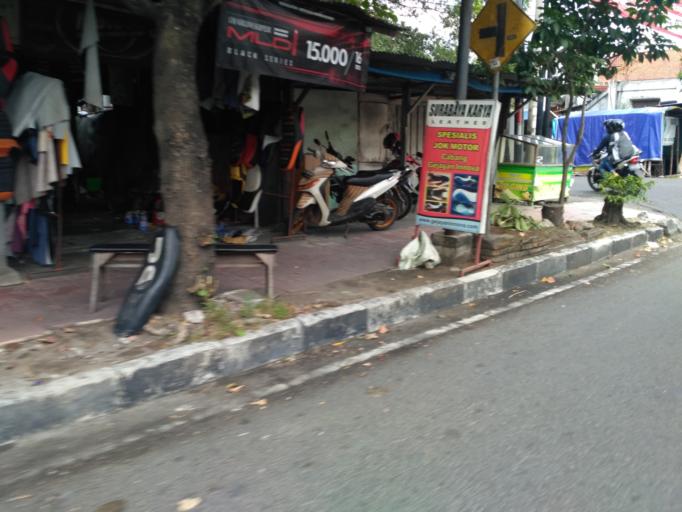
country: ID
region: Daerah Istimewa Yogyakarta
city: Depok
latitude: -7.7616
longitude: 110.3942
